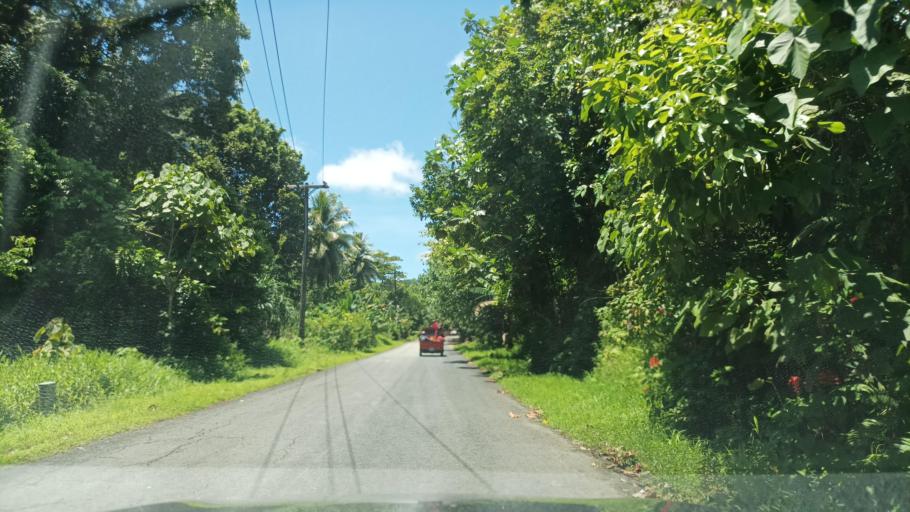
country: FM
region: Pohnpei
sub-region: Kolonia Municipality
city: Kolonia
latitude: 6.9379
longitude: 158.2785
